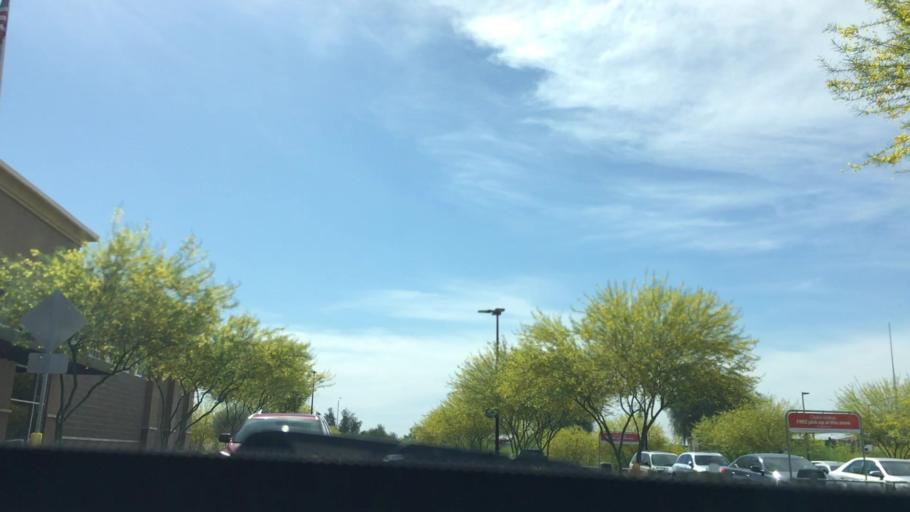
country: US
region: Arizona
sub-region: Maricopa County
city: Peoria
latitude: 33.6094
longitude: -112.2182
